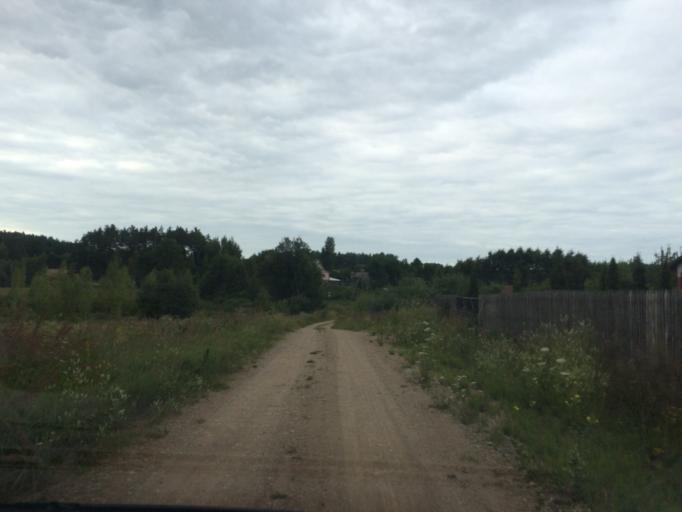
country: LV
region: Rezekne
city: Rezekne
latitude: 56.5874
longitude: 27.4110
